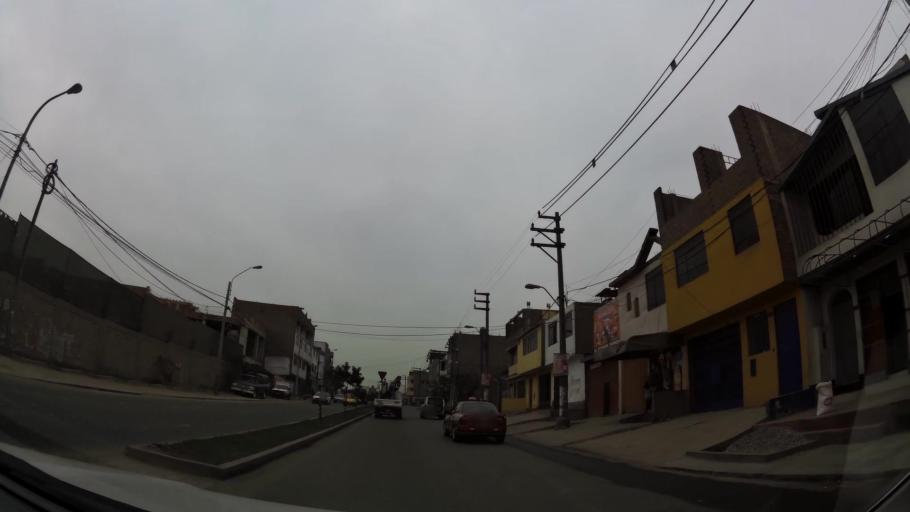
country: PE
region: Lima
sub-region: Lima
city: Independencia
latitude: -11.9832
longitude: -76.9933
